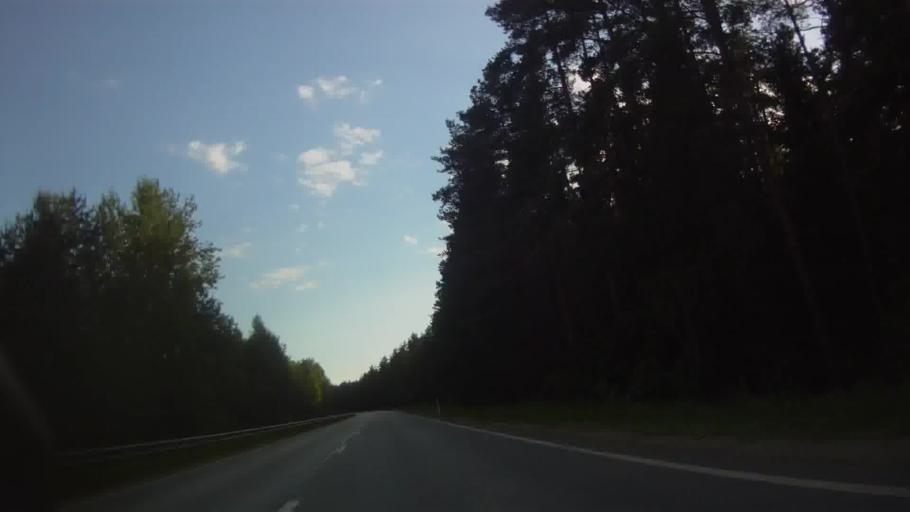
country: LV
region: Varaklani
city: Varaklani
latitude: 56.5754
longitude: 26.6636
